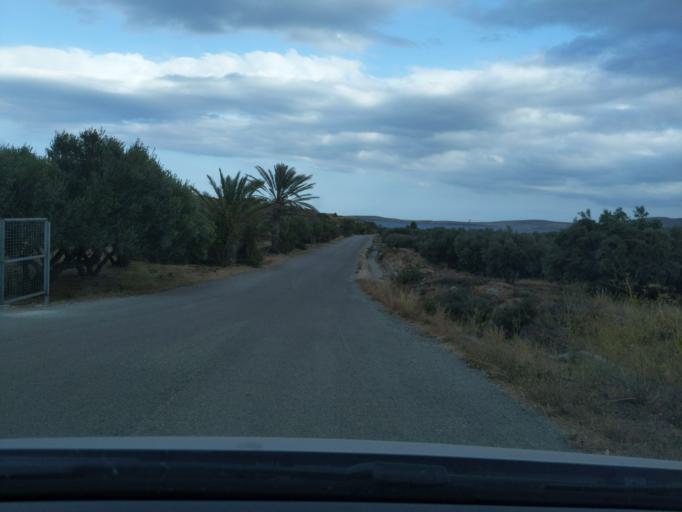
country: GR
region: Crete
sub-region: Nomos Lasithiou
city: Palekastro
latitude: 35.2161
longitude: 26.2647
